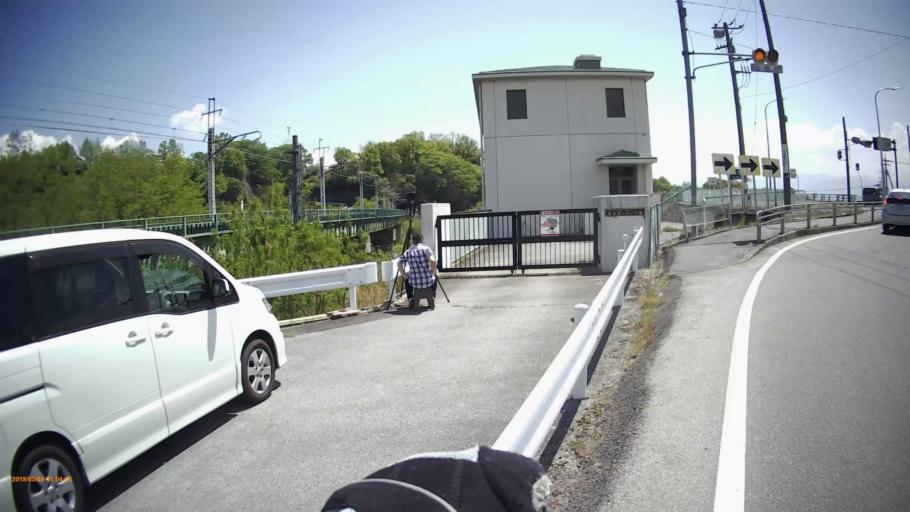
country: JP
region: Yamanashi
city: Nirasaki
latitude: 35.6985
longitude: 138.4661
